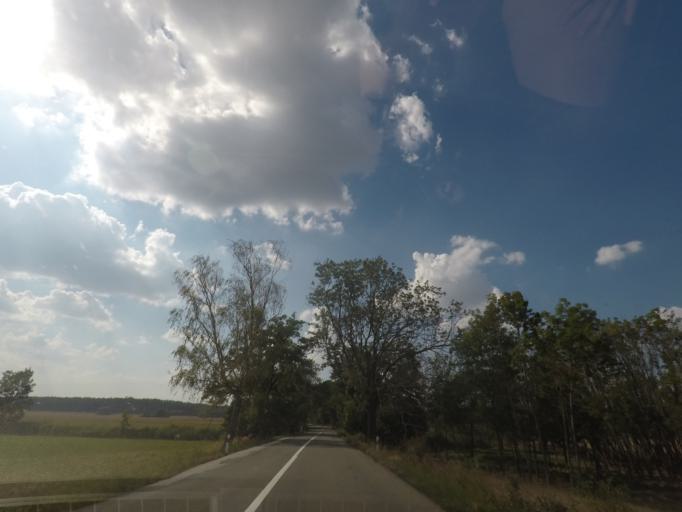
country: CZ
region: Kralovehradecky
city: Trebechovice pod Orebem
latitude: 50.2161
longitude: 15.9880
